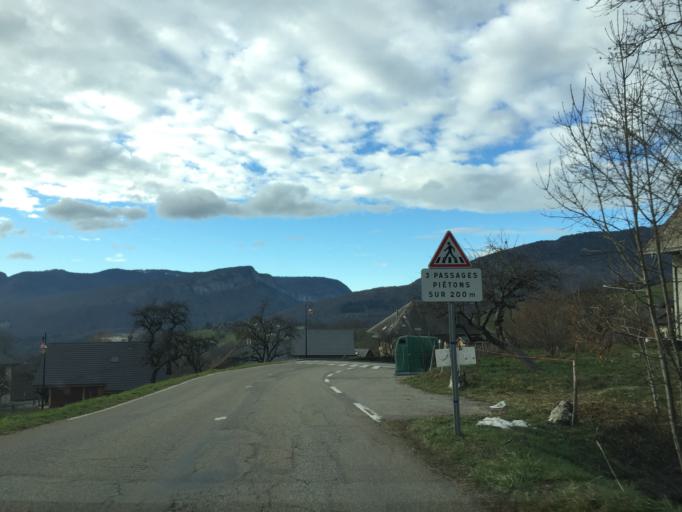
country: FR
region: Rhone-Alpes
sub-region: Departement de la Haute-Savoie
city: Doussard
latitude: 45.7369
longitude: 6.1417
